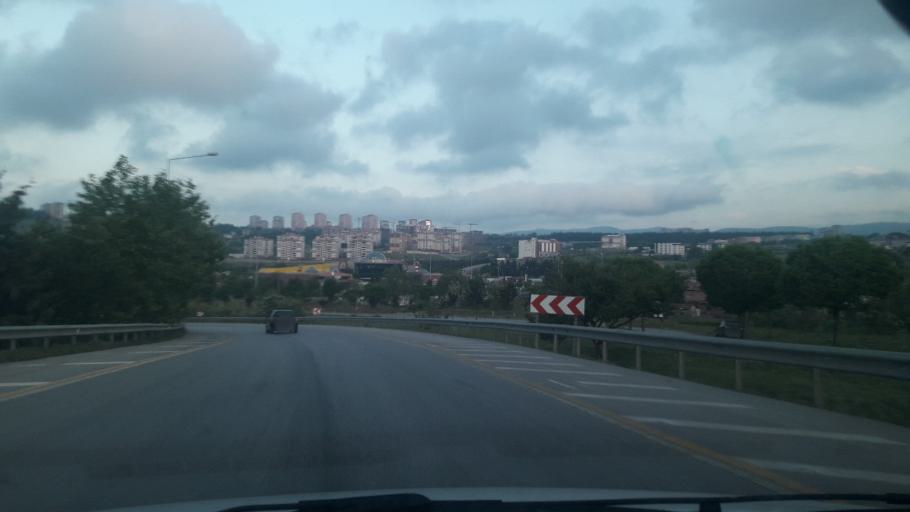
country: TR
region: Samsun
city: Samsun
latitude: 41.2900
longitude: 36.2847
